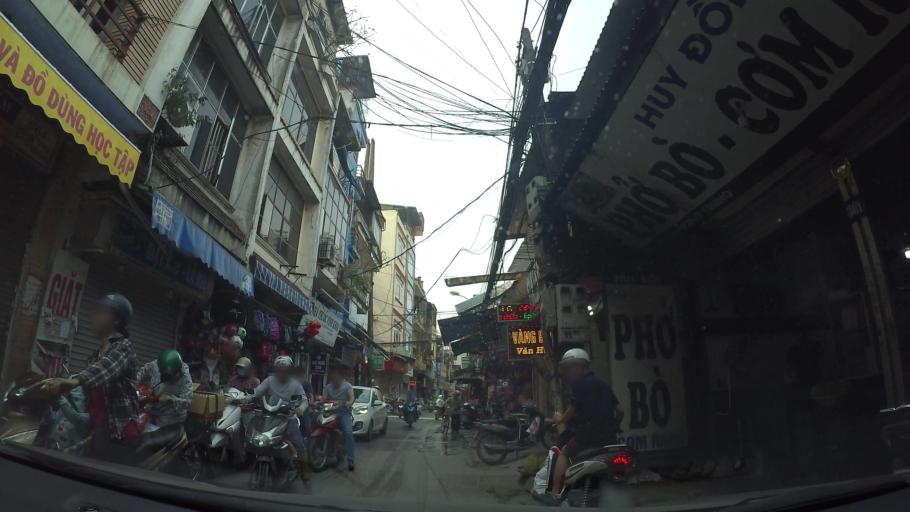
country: VN
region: Ha Noi
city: Thanh Xuan
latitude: 20.9925
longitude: 105.8172
